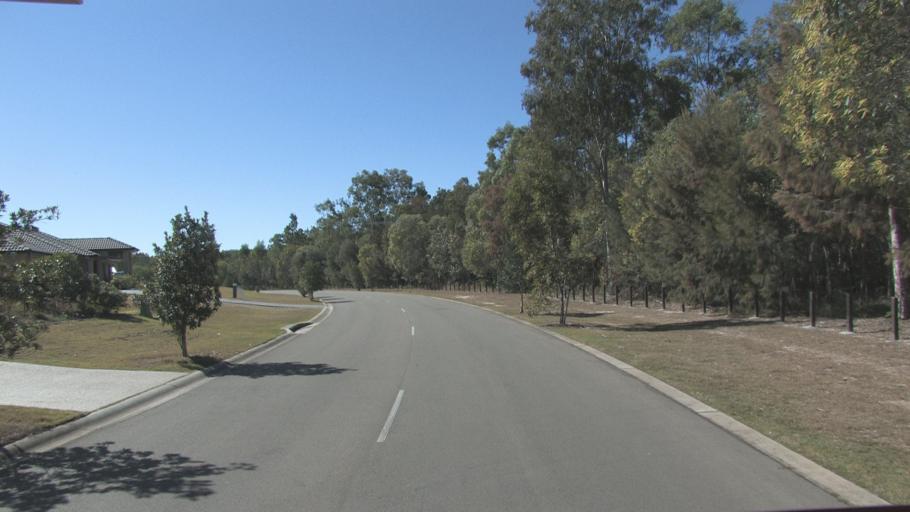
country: AU
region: Queensland
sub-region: Logan
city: North Maclean
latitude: -27.7545
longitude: 152.9654
